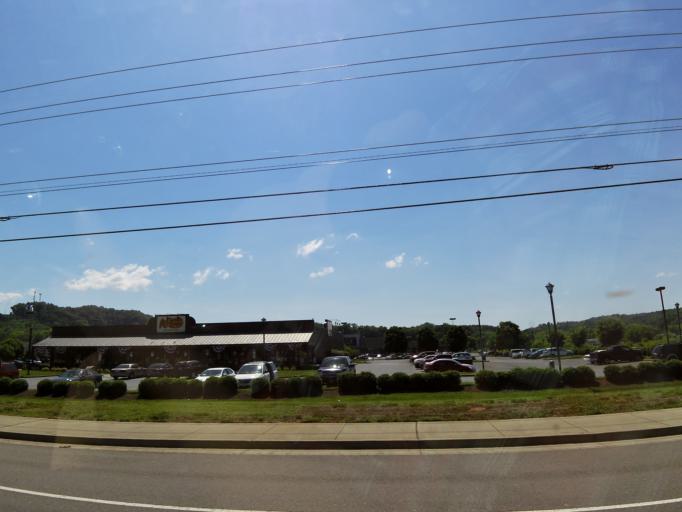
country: US
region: Tennessee
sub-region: Sevier County
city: Sevierville
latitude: 35.8802
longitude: -83.5725
